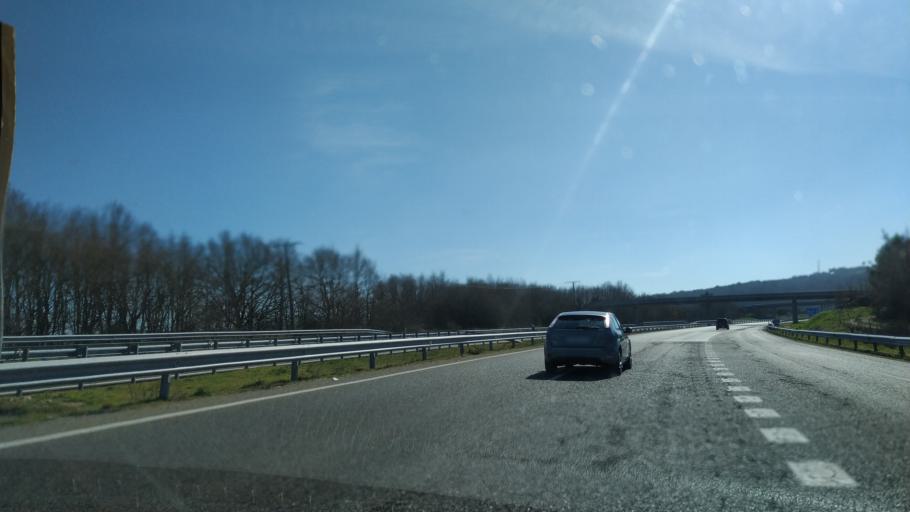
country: ES
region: Galicia
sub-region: Provincia de Ourense
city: Taboadela
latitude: 42.2461
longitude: -7.8604
